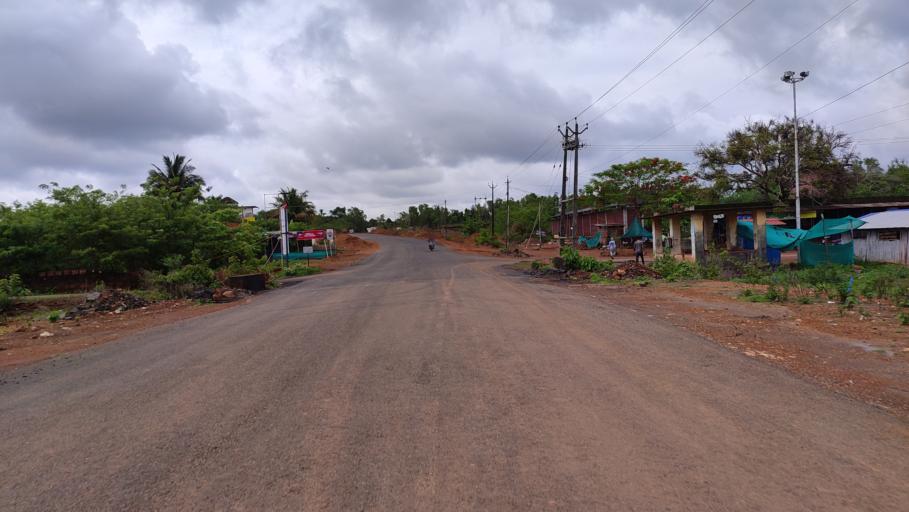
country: IN
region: Kerala
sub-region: Kasaragod District
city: Kasaragod
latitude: 12.5562
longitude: 75.0699
